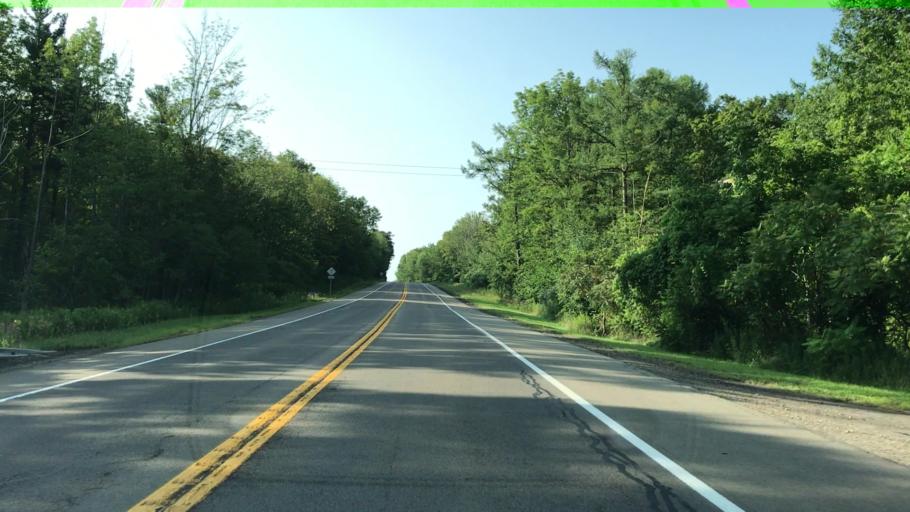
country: US
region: New York
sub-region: Chautauqua County
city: Fredonia
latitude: 42.3709
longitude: -79.3143
